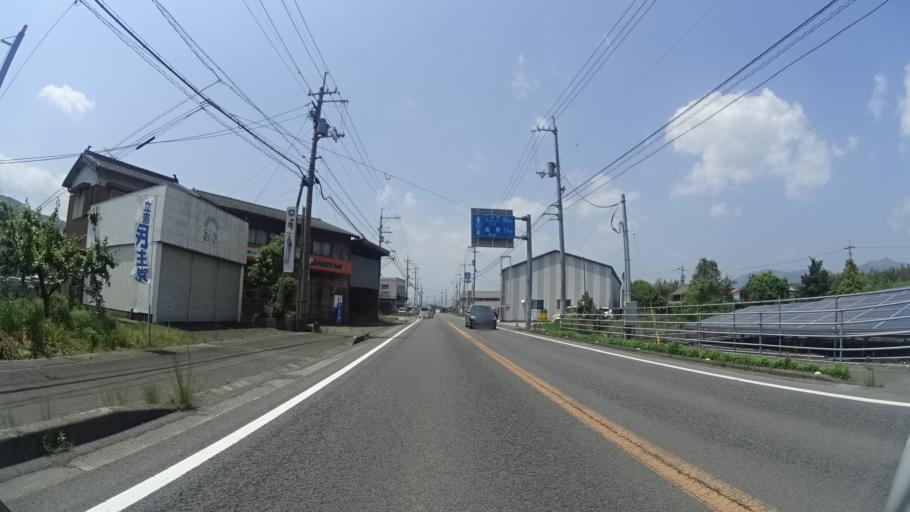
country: JP
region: Tokushima
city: Kamojimacho-jogejima
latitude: 34.0636
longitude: 134.2796
